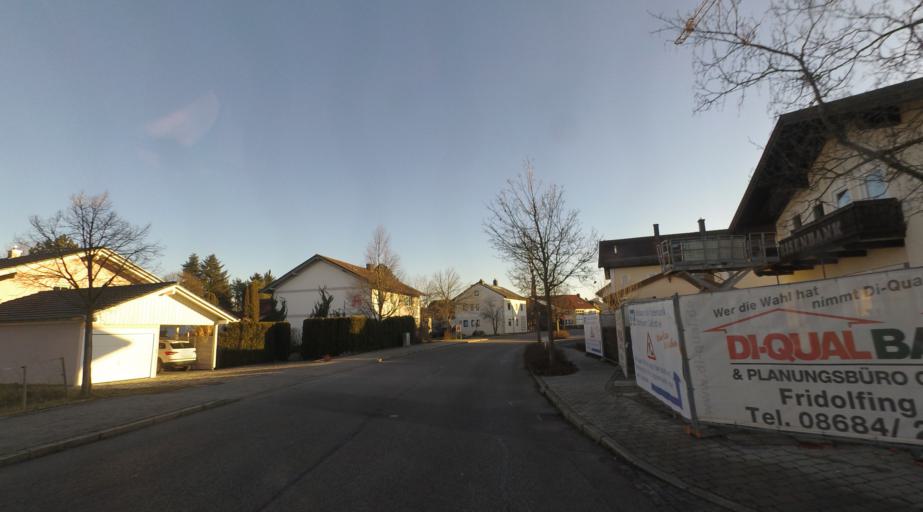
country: DE
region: Bavaria
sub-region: Upper Bavaria
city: Kirchanschoring
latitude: 47.9555
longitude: 12.8330
